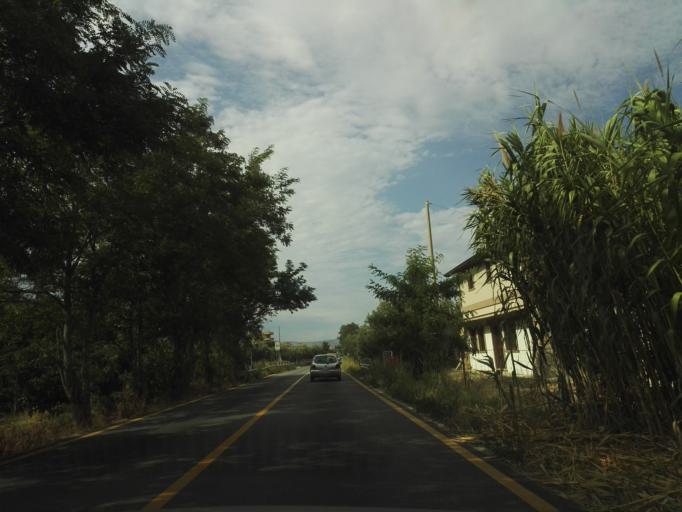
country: IT
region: Calabria
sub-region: Provincia di Catanzaro
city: Marina di Davoli
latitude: 38.6436
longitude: 16.5487
